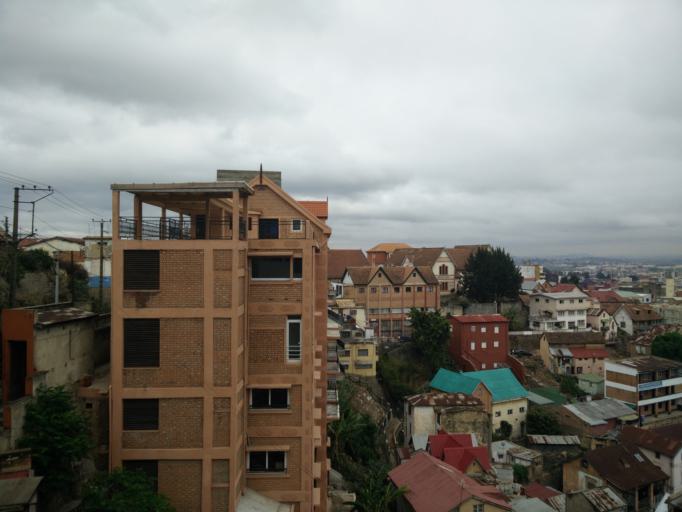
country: MG
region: Analamanga
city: Antananarivo
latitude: -18.9139
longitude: 47.5291
